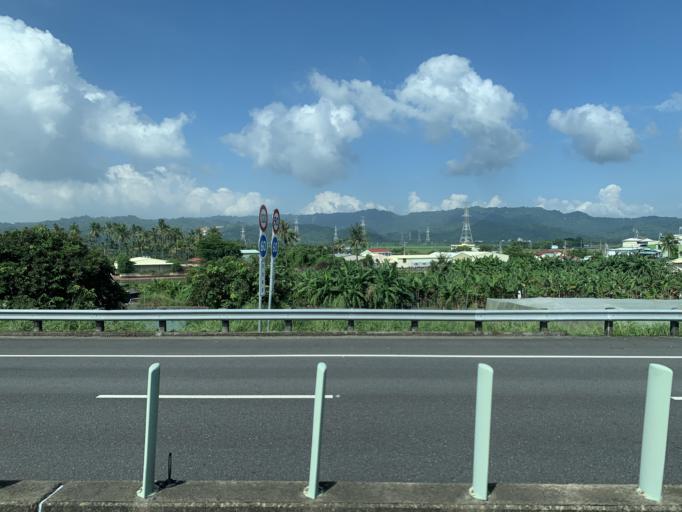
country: TW
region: Taiwan
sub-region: Pingtung
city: Pingtung
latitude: 22.8133
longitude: 120.4858
